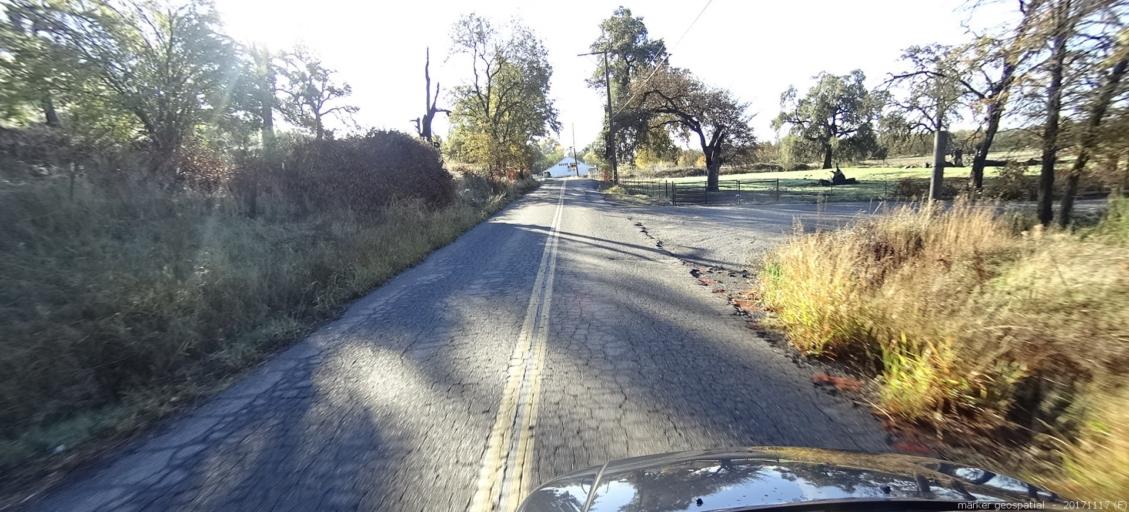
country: US
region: California
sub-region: Shasta County
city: Cottonwood
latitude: 40.4000
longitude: -122.1813
